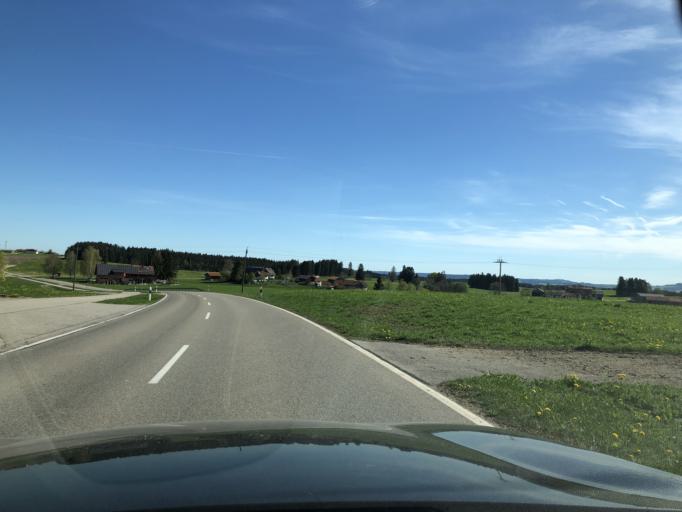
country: DE
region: Bavaria
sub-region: Swabia
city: Wald
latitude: 47.7026
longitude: 10.5500
